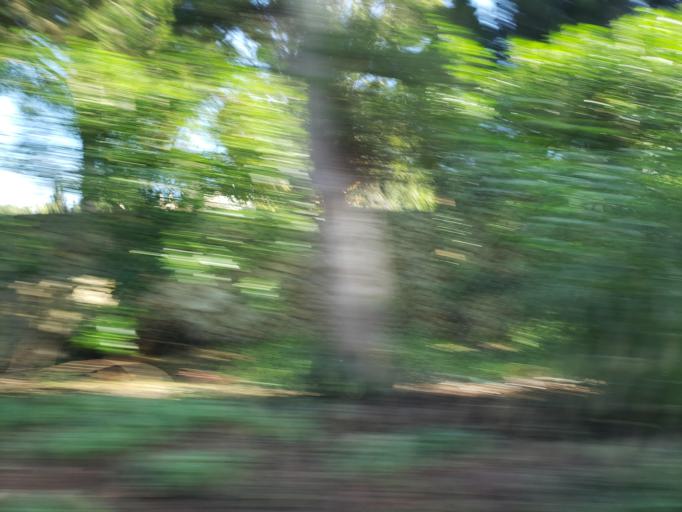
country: PT
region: Faro
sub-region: Portimao
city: Alvor
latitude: 37.1844
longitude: -8.5857
